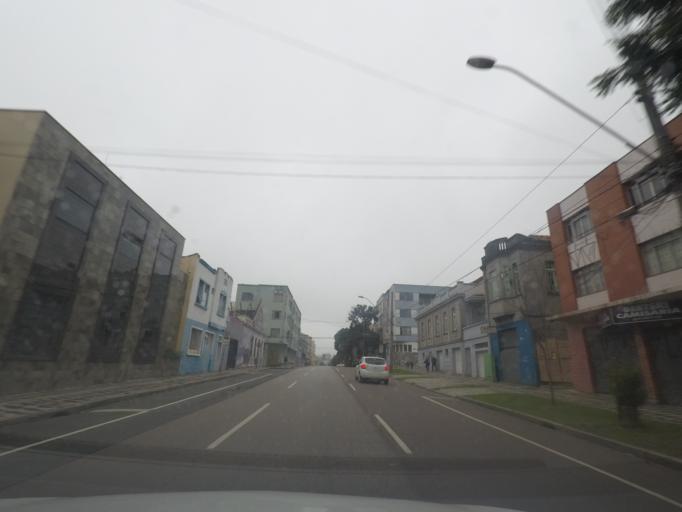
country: BR
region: Parana
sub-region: Curitiba
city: Curitiba
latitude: -25.4289
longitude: -49.2756
